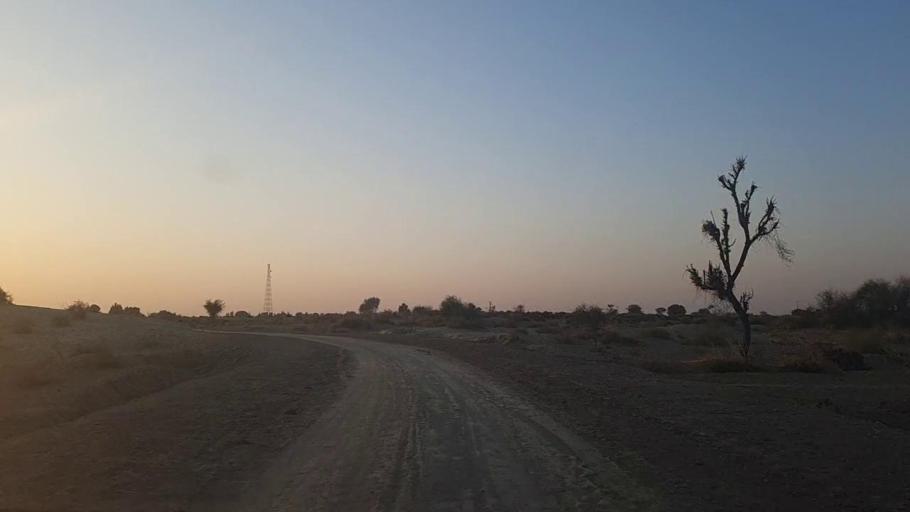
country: PK
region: Sindh
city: Jam Sahib
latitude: 26.3666
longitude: 68.7155
